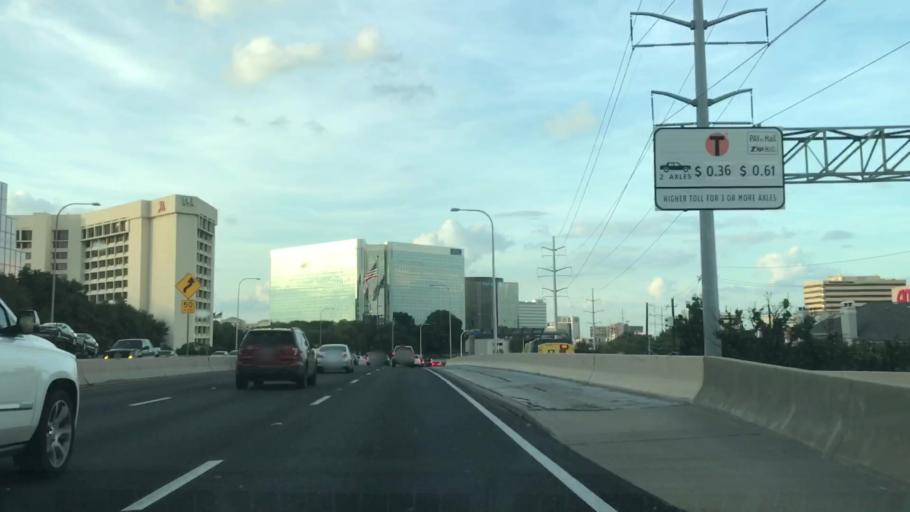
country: US
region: Texas
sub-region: Dallas County
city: Addison
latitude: 32.9492
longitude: -96.8233
